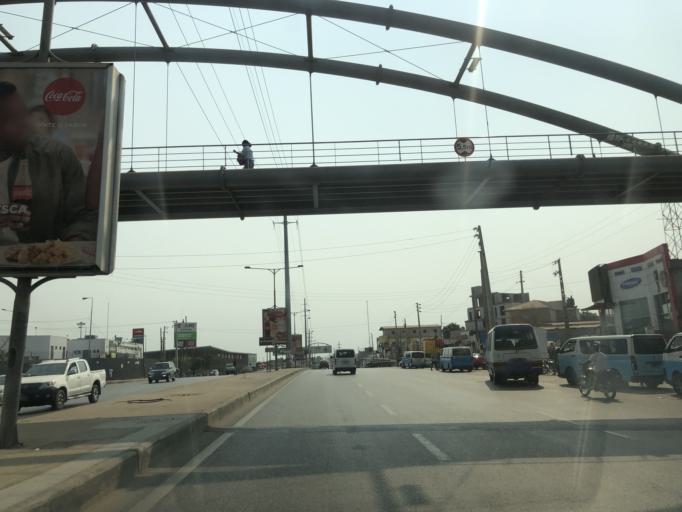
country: AO
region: Luanda
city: Luanda
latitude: -8.8946
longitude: 13.2284
